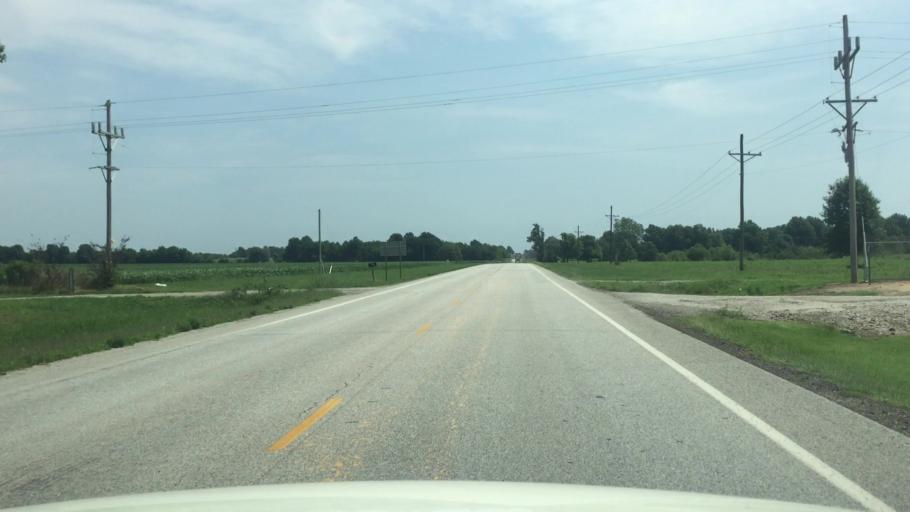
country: US
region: Kansas
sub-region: Cherokee County
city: Columbus
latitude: 37.1781
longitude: -94.8140
